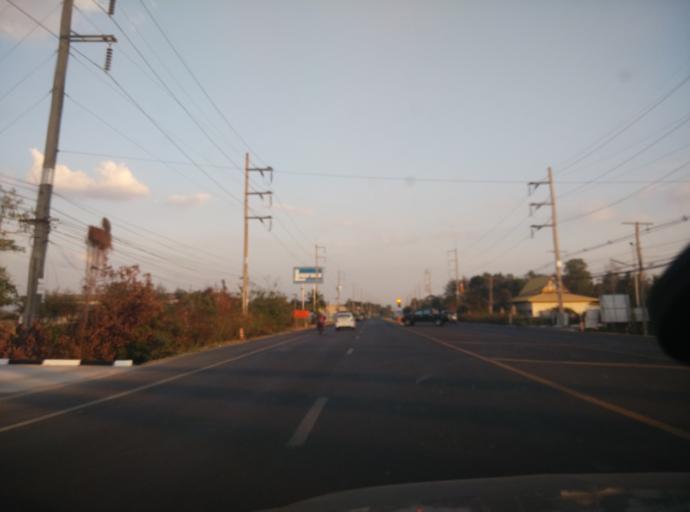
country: TH
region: Sisaket
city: Si Sa Ket
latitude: 15.1333
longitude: 104.2713
